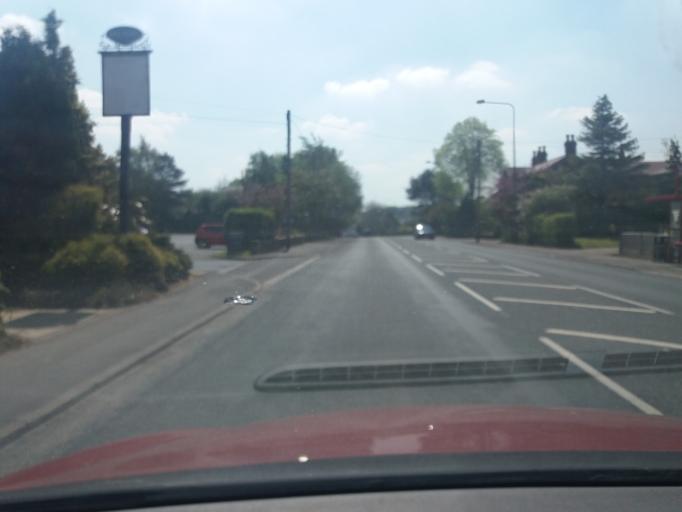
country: GB
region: England
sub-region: Lancashire
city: Clayton-le-Woods
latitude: 53.7017
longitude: -2.6396
